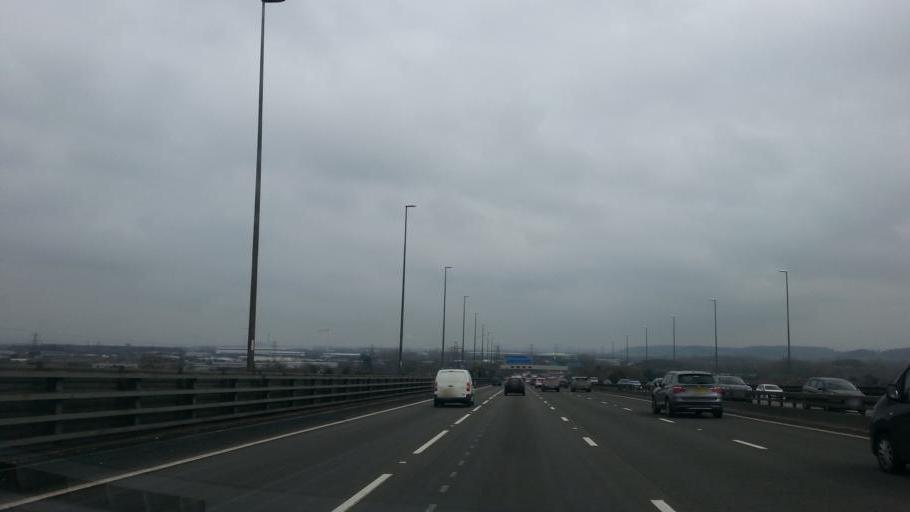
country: GB
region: England
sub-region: North Somerset
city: Easton-in-Gordano
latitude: 51.4915
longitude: -2.6902
